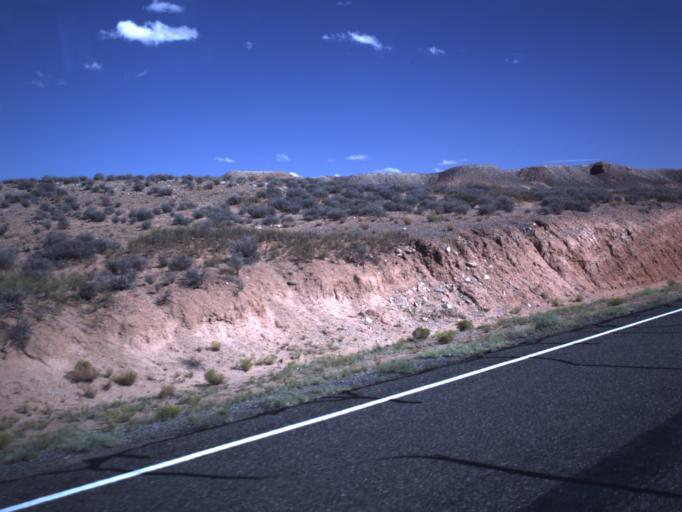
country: US
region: Utah
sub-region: Wayne County
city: Loa
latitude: 38.0943
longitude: -110.6200
